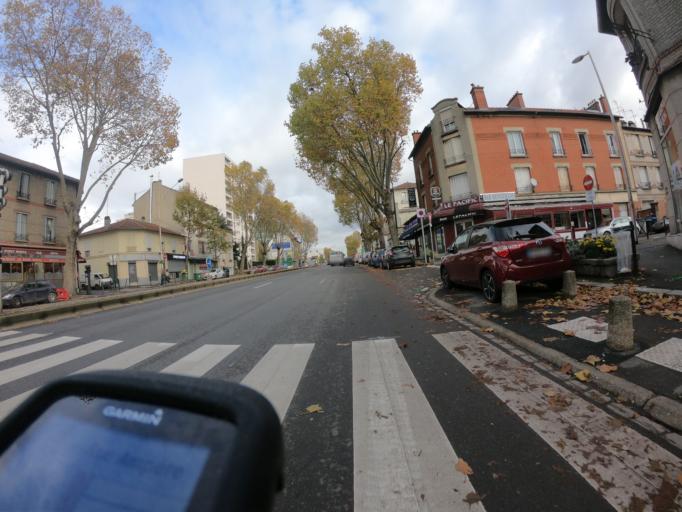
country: FR
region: Ile-de-France
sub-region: Departement du Val-de-Marne
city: Arcueil
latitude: 48.7946
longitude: 2.3214
